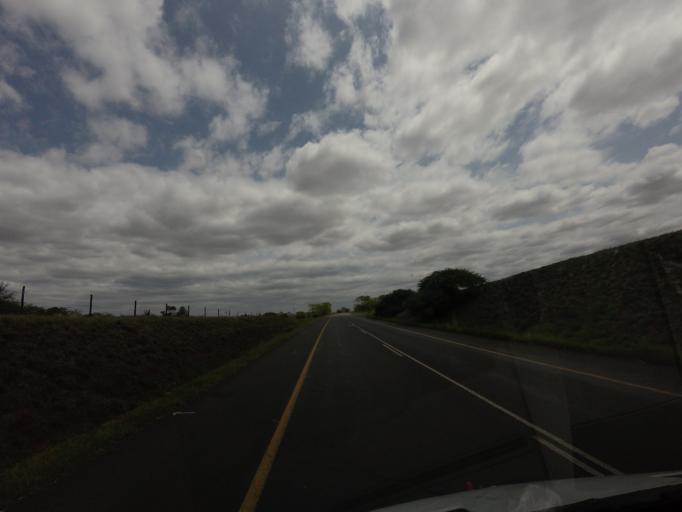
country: ZA
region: KwaZulu-Natal
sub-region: uMkhanyakude District Municipality
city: Hluhluwe
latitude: -28.0443
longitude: 32.2479
